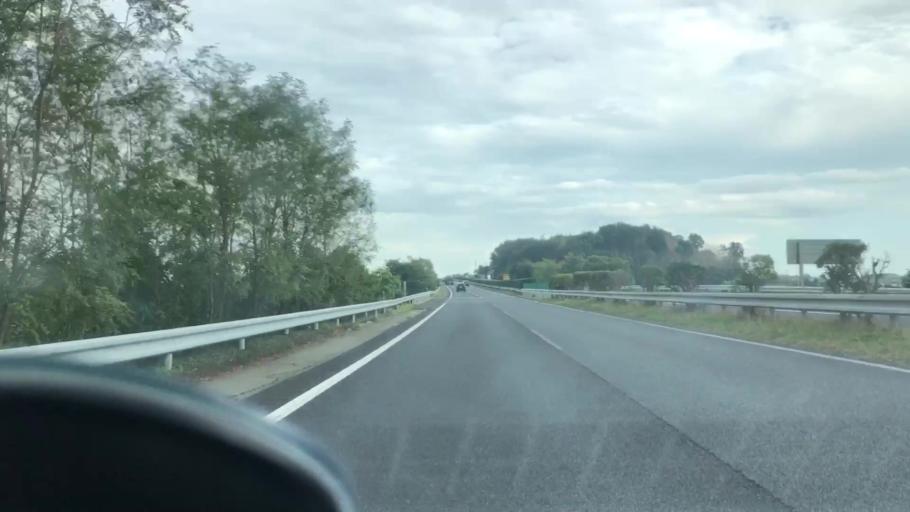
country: JP
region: Hyogo
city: Yashiro
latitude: 34.9353
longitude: 134.8852
